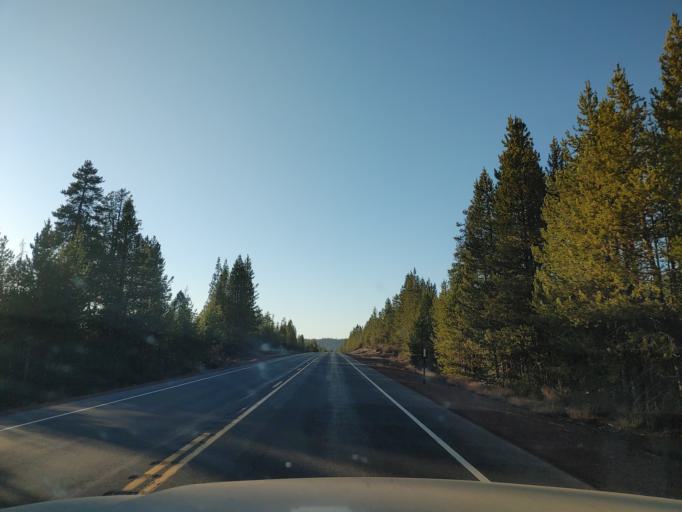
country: US
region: Oregon
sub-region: Deschutes County
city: La Pine
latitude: 43.4235
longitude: -121.8447
